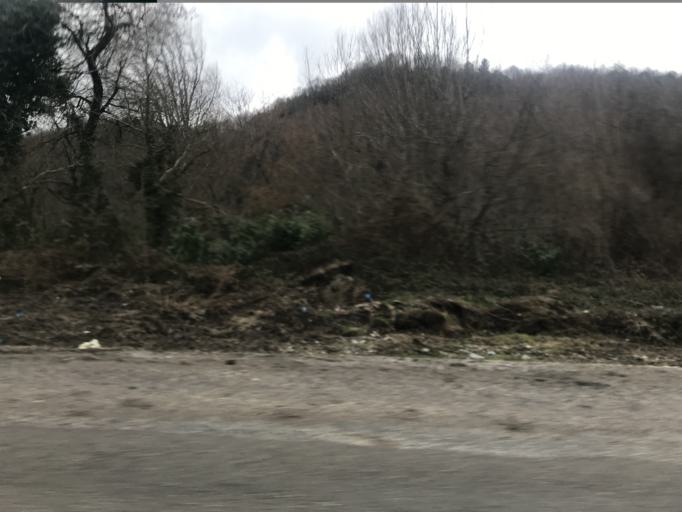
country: TR
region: Bartin
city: Amasra
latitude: 41.6974
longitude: 32.3840
